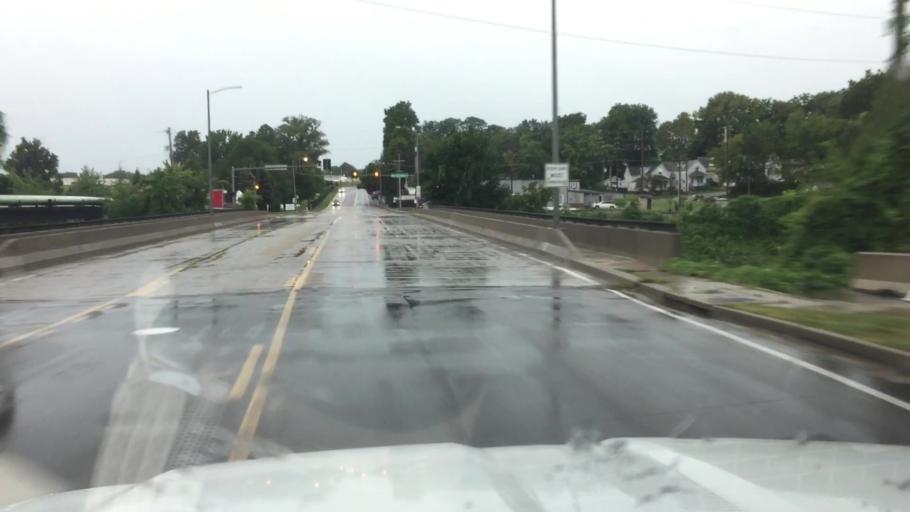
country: US
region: Missouri
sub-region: Saint Louis County
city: Lemay
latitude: 38.5386
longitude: -90.2681
